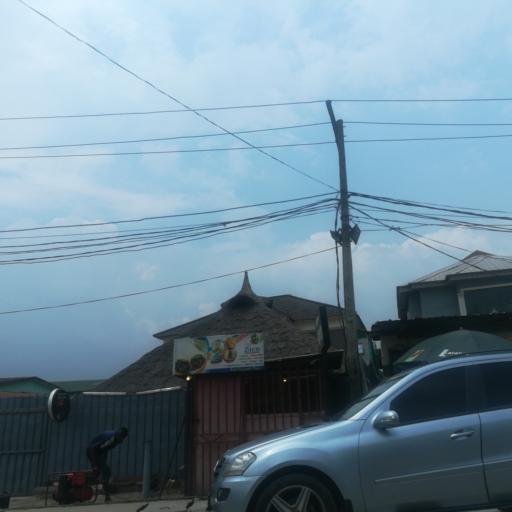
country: NG
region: Lagos
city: Ojota
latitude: 6.5745
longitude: 3.4012
